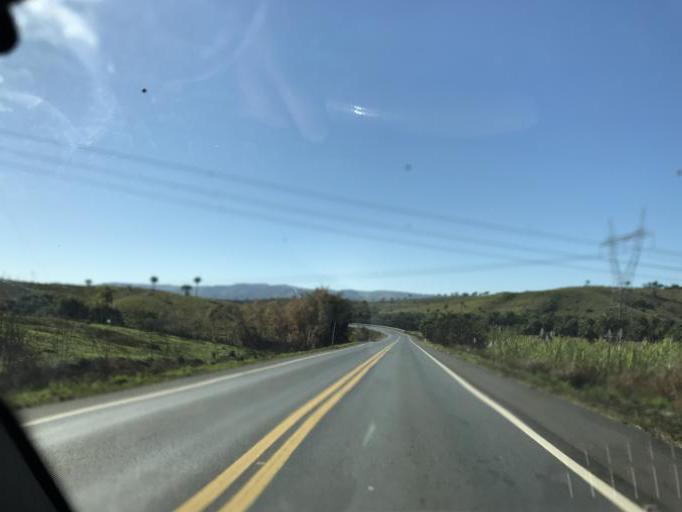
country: BR
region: Minas Gerais
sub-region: Bambui
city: Bambui
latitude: -19.8440
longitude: -45.9996
